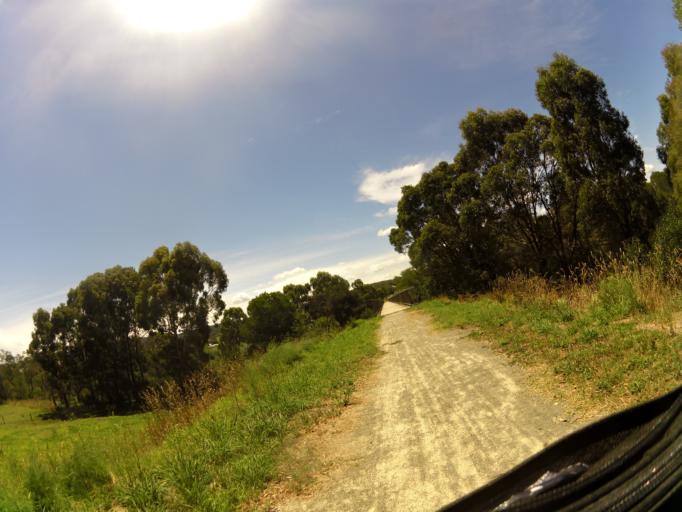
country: AU
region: Victoria
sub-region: East Gippsland
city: Lakes Entrance
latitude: -37.7116
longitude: 147.8329
